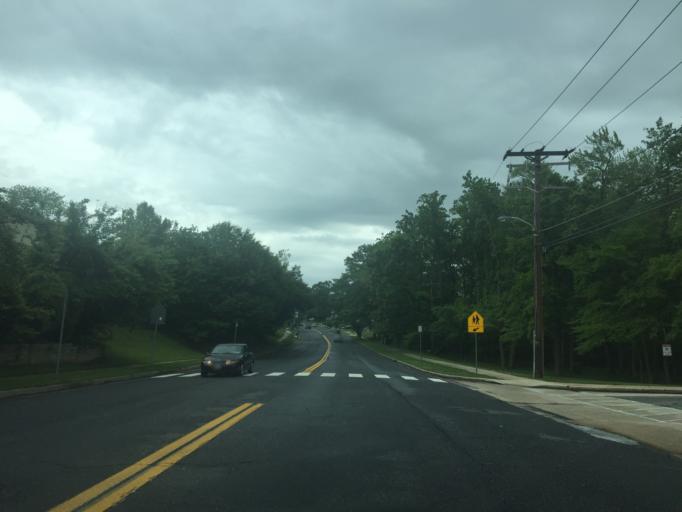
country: US
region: Maryland
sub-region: Baltimore County
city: Perry Hall
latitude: 39.3935
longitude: -76.4632
